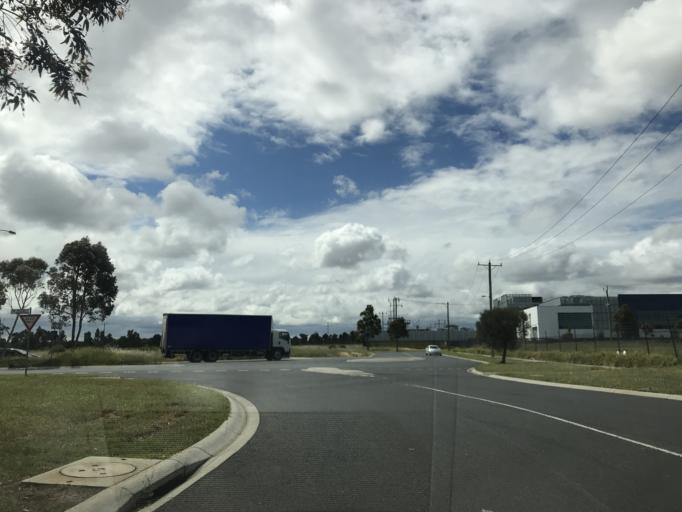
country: AU
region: Victoria
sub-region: Brimbank
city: Derrimut
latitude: -37.8028
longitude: 144.7723
